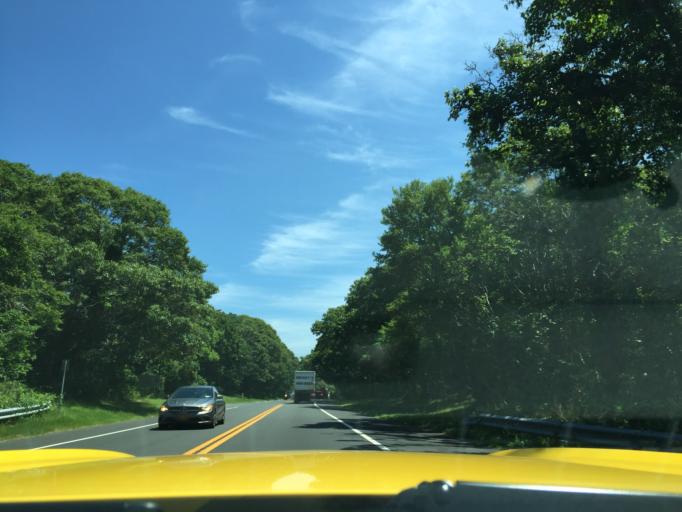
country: US
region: New York
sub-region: Suffolk County
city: Montauk
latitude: 41.0301
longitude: -71.9760
